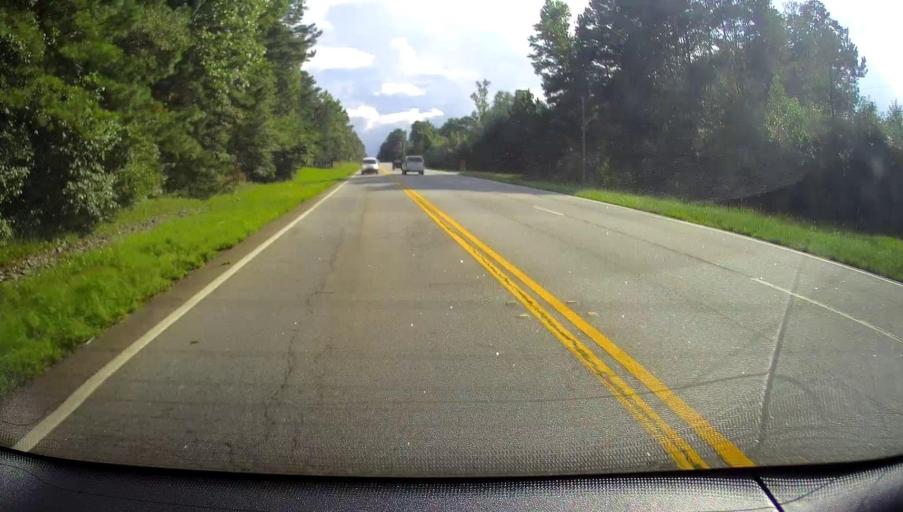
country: US
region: Georgia
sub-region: Coweta County
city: Senoia
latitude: 33.3164
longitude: -84.5246
